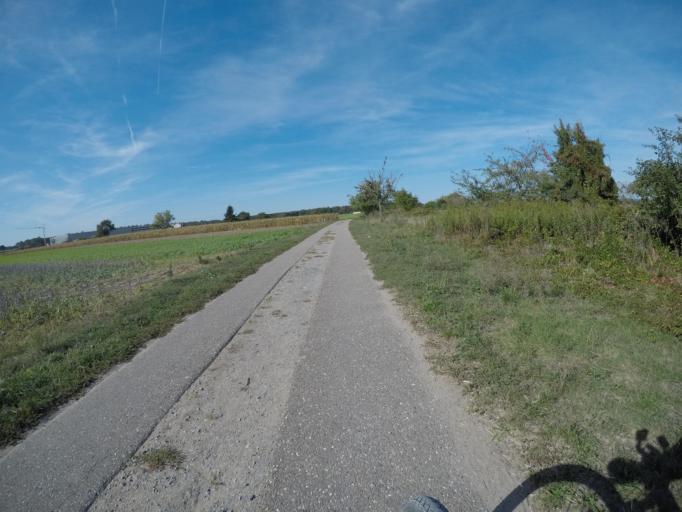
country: DE
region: Baden-Wuerttemberg
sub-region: Karlsruhe Region
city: Kronau
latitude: 49.2240
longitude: 8.6217
